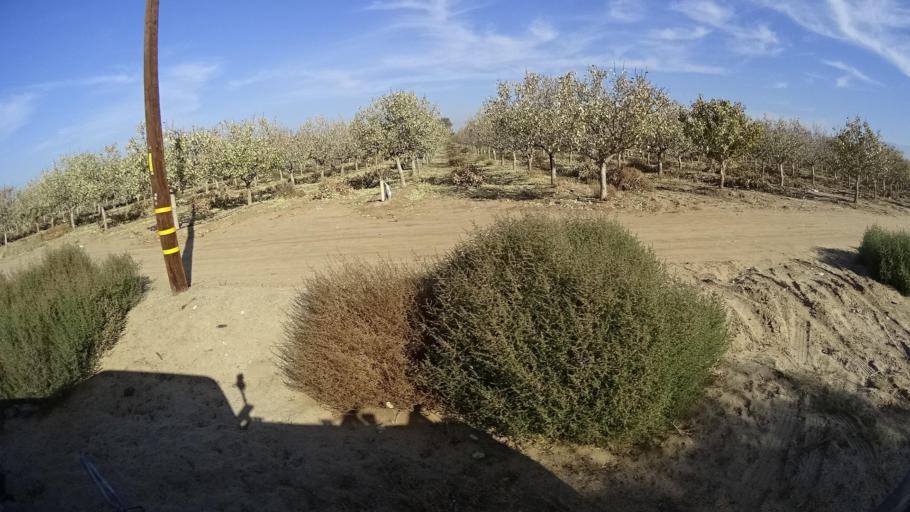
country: US
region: California
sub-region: Kern County
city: Lamont
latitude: 35.3253
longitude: -118.9068
